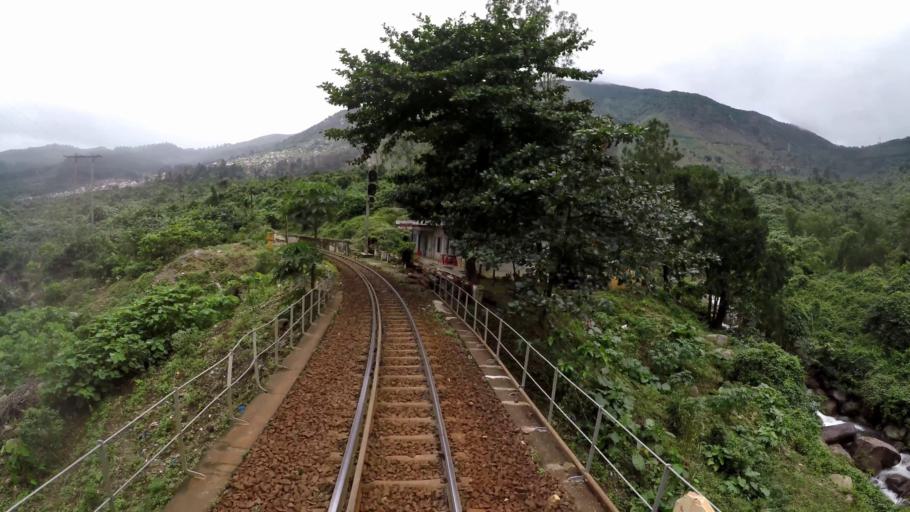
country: VN
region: Da Nang
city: Lien Chieu
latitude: 16.1719
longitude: 108.1370
